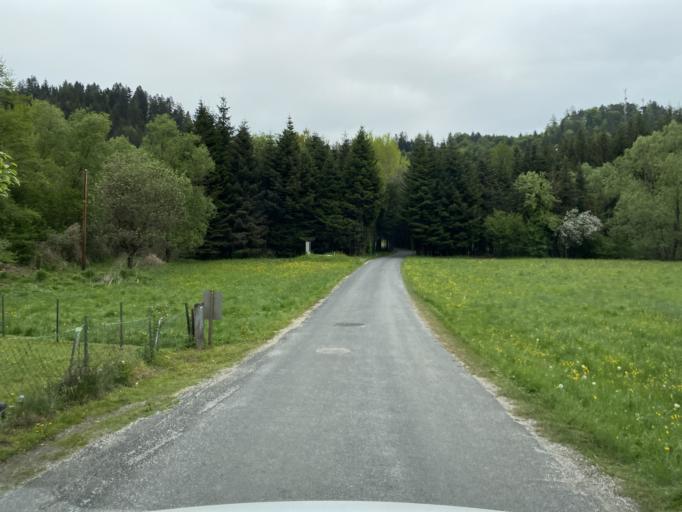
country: AT
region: Styria
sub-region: Politischer Bezirk Weiz
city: Koglhof
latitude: 47.3118
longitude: 15.6864
